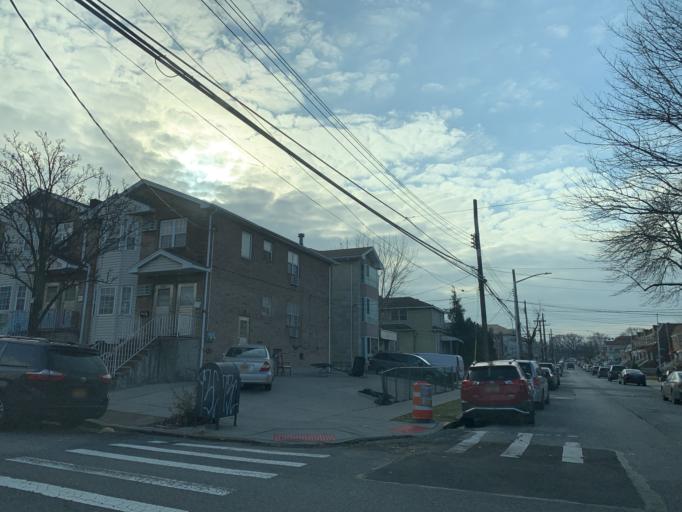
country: US
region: New York
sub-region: Queens County
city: Jamaica
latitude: 40.7468
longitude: -73.8331
